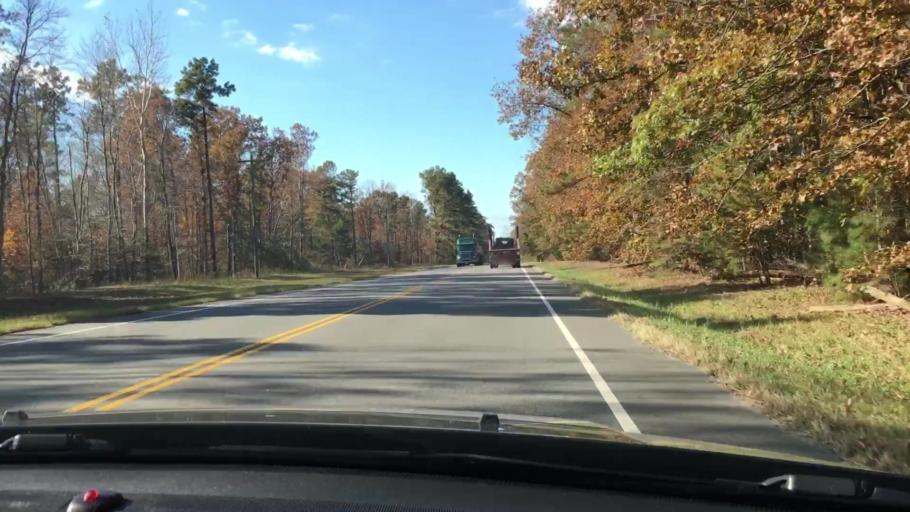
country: US
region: Virginia
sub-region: King William County
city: Central Garage
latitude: 37.7954
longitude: -77.2469
